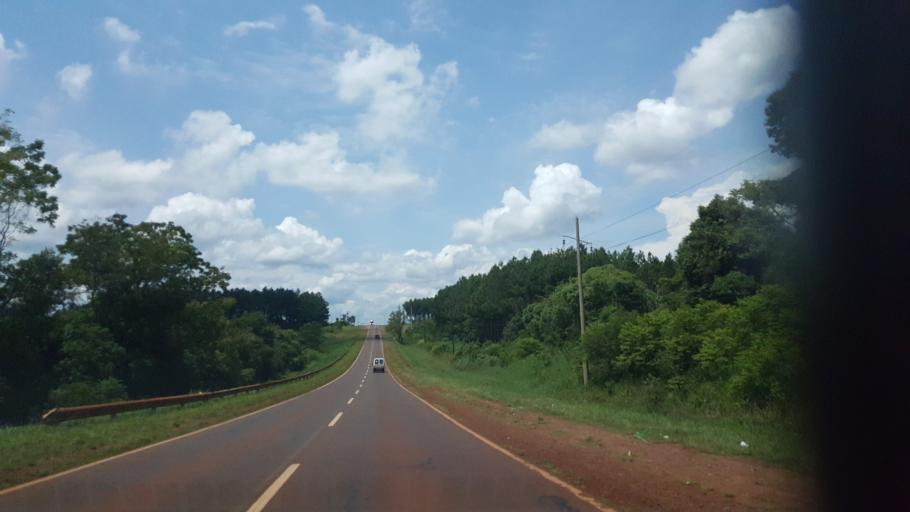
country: AR
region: Misiones
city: Puerto Rico
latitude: -26.8208
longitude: -55.0071
